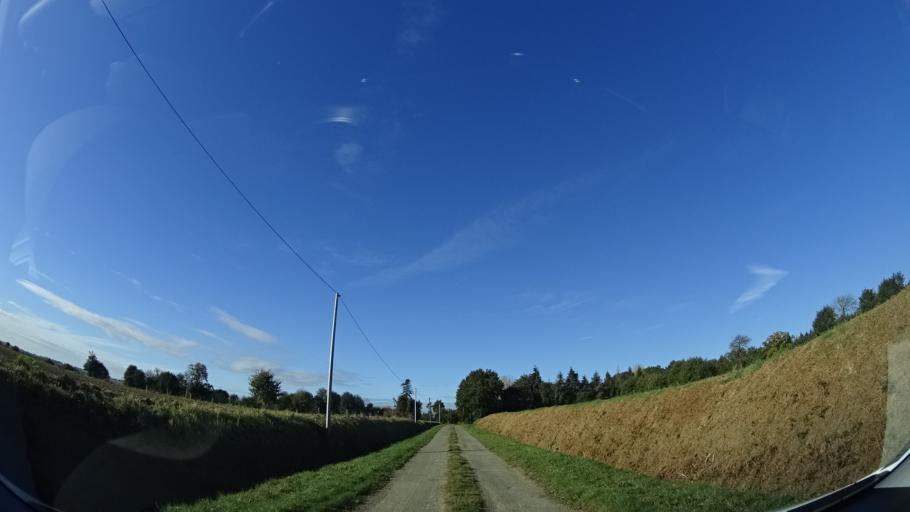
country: FR
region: Brittany
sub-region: Departement d'Ille-et-Vilaine
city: La Meziere
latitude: 48.2057
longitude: -1.7691
